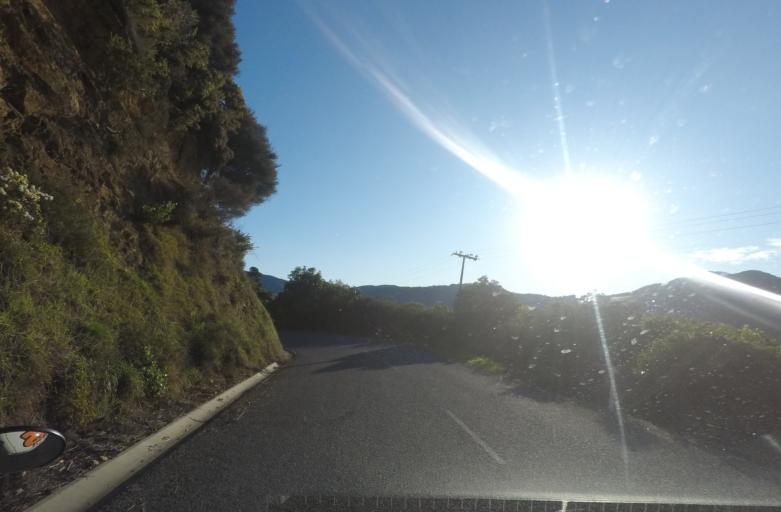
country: NZ
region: Marlborough
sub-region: Marlborough District
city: Picton
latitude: -41.2690
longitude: 173.9714
